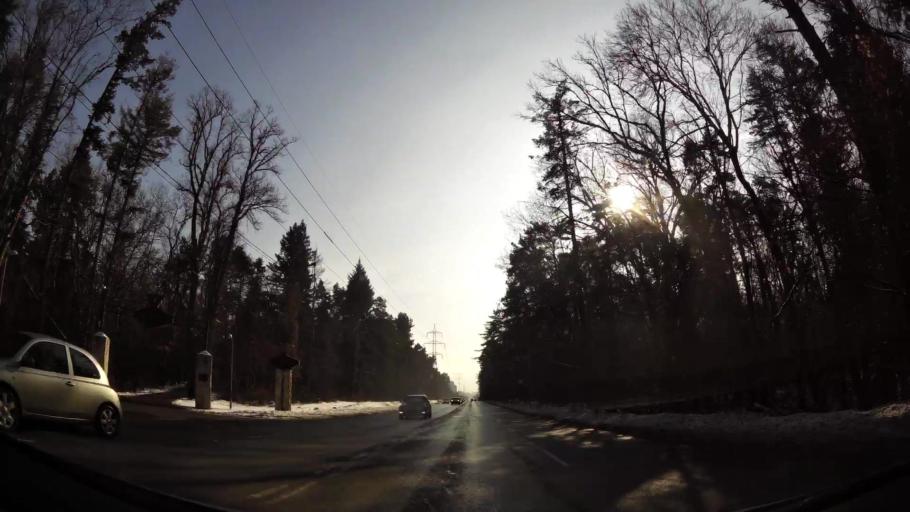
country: BG
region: Sofia-Capital
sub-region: Stolichna Obshtina
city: Sofia
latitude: 42.6637
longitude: 23.3371
